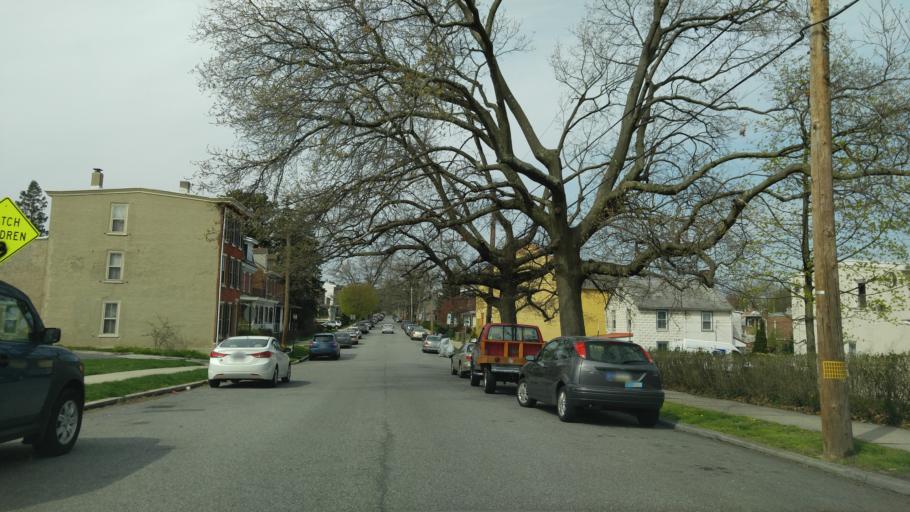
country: US
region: Pennsylvania
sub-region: Chester County
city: Phoenixville
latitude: 40.1311
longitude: -75.5117
